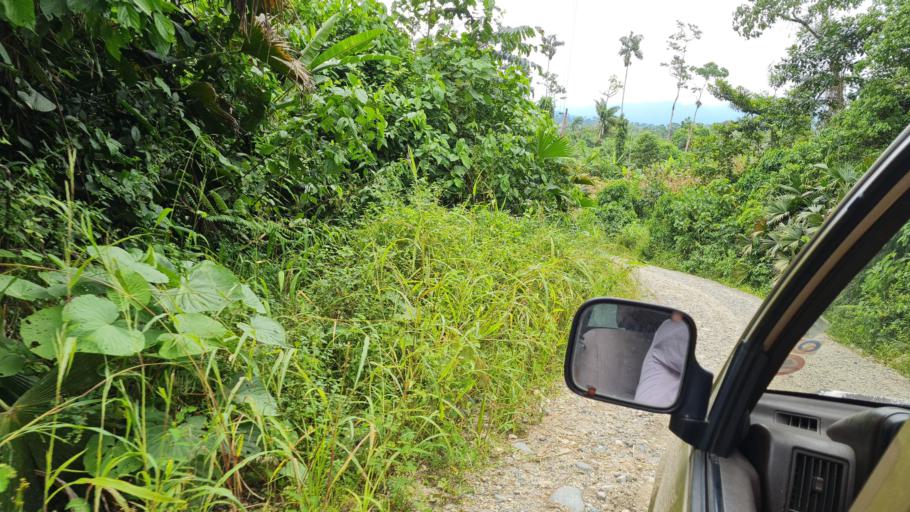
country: EC
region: Napo
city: Tena
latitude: -0.9998
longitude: -77.7601
